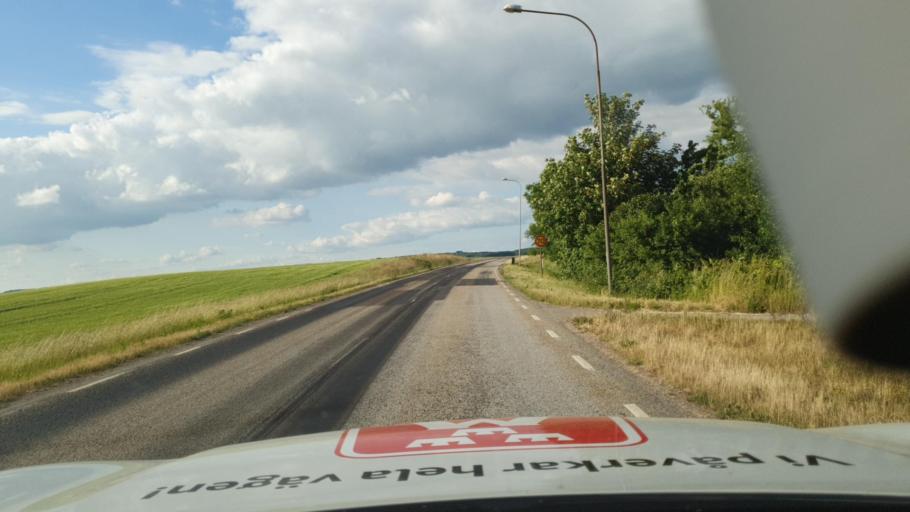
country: SE
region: Skane
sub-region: Skurups Kommun
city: Rydsgard
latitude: 55.4855
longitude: 13.5925
